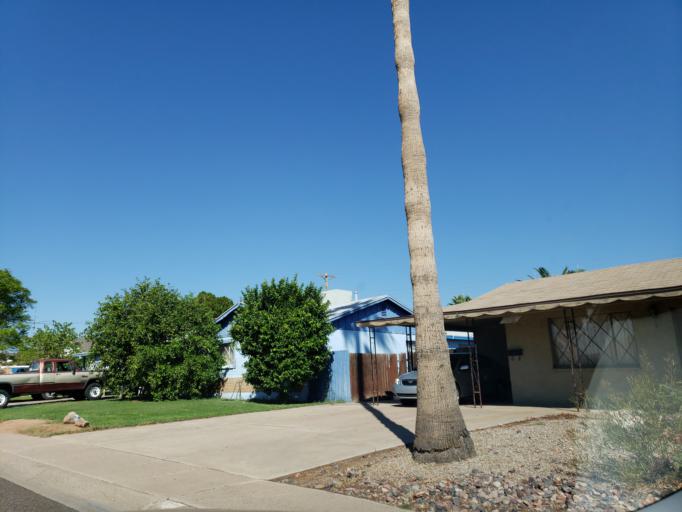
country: US
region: Arizona
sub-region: Maricopa County
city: Tempe
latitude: 33.4586
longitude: -111.9224
